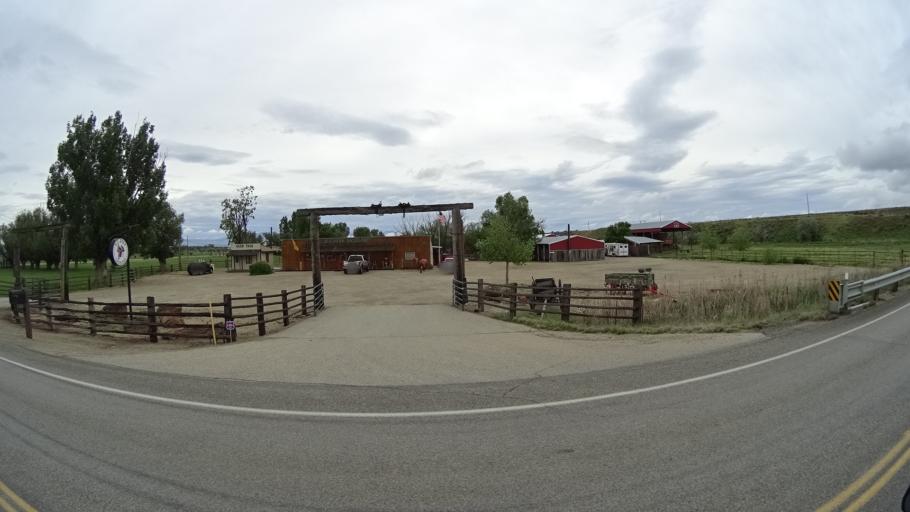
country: US
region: Idaho
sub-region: Ada County
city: Star
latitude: 43.6694
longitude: -116.4936
